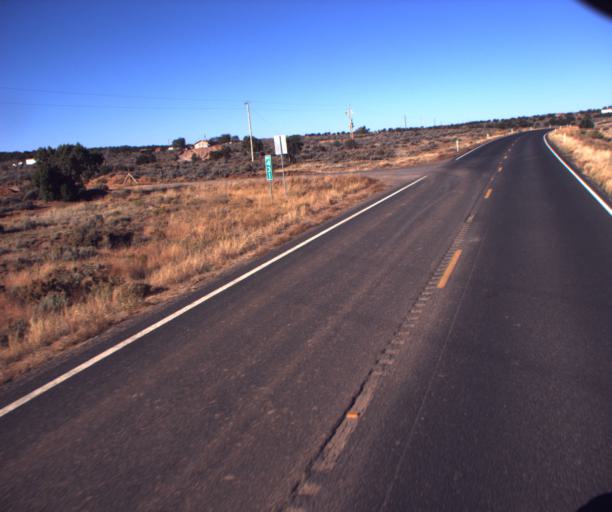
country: US
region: Arizona
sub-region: Apache County
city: Ganado
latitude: 35.7613
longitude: -109.7802
